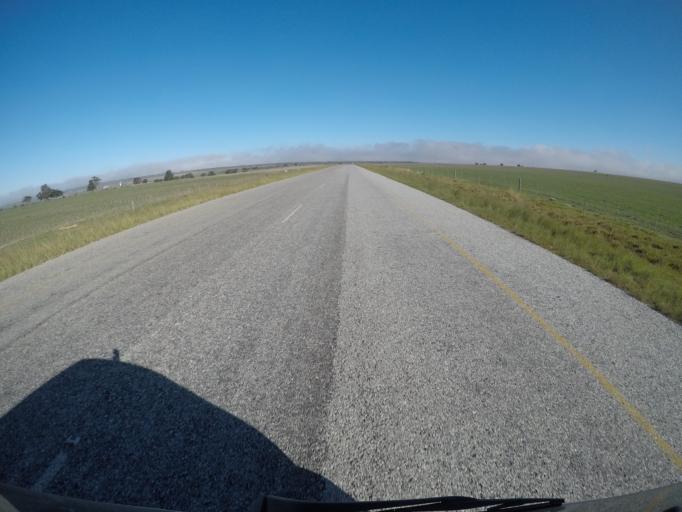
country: ZA
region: Western Cape
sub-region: Eden District Municipality
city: Mossel Bay
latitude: -34.1740
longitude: 22.0150
